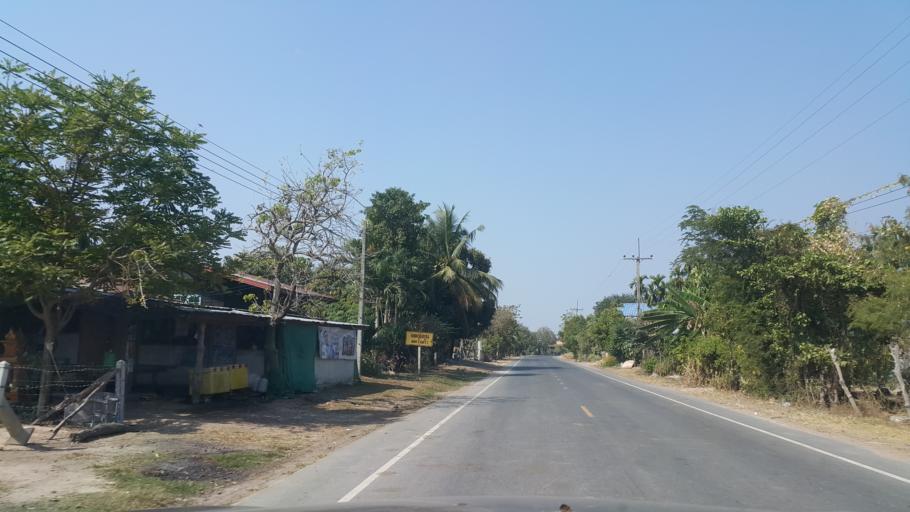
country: TH
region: Surin
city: Khwao Sinarin
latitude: 15.0421
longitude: 103.4310
